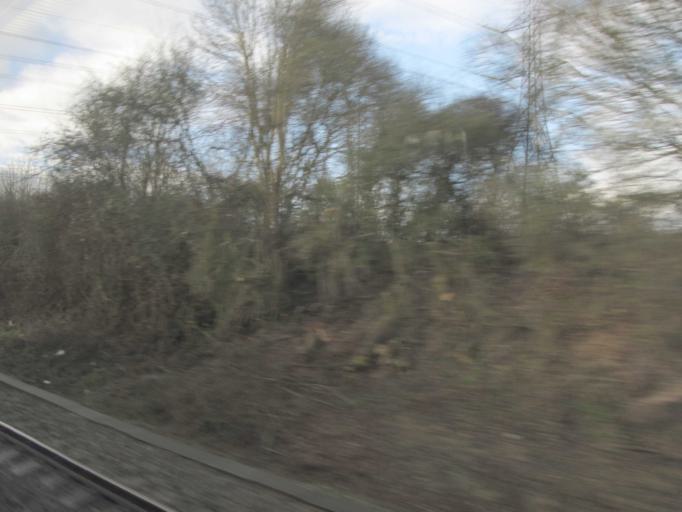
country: GB
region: England
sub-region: West Berkshire
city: Stratfield Mortimer
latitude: 51.3358
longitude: -1.0620
